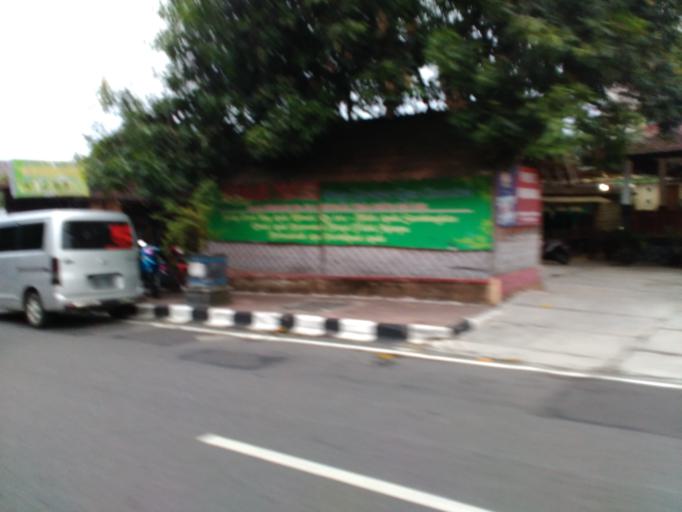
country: ID
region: Central Java
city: Boyolali
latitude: -7.5315
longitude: 110.5934
